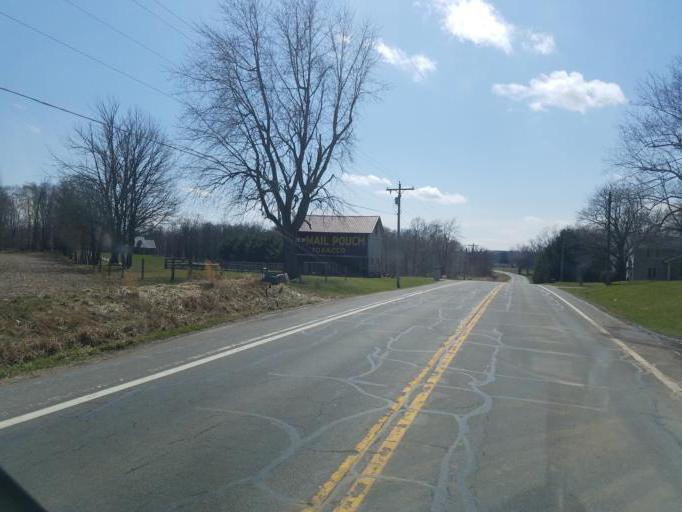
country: US
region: Ohio
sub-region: Richland County
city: Lexington
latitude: 40.6577
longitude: -82.6177
